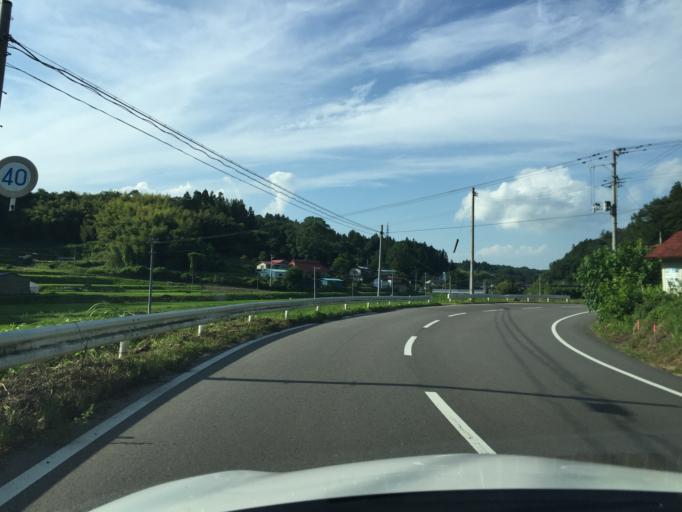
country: JP
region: Fukushima
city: Miharu
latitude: 37.3471
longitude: 140.5088
